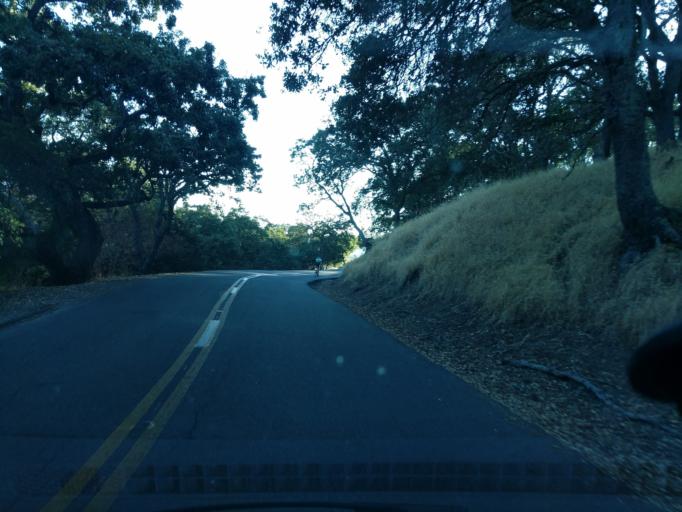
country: US
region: California
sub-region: Contra Costa County
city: Diablo
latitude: 37.8432
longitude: -121.9420
